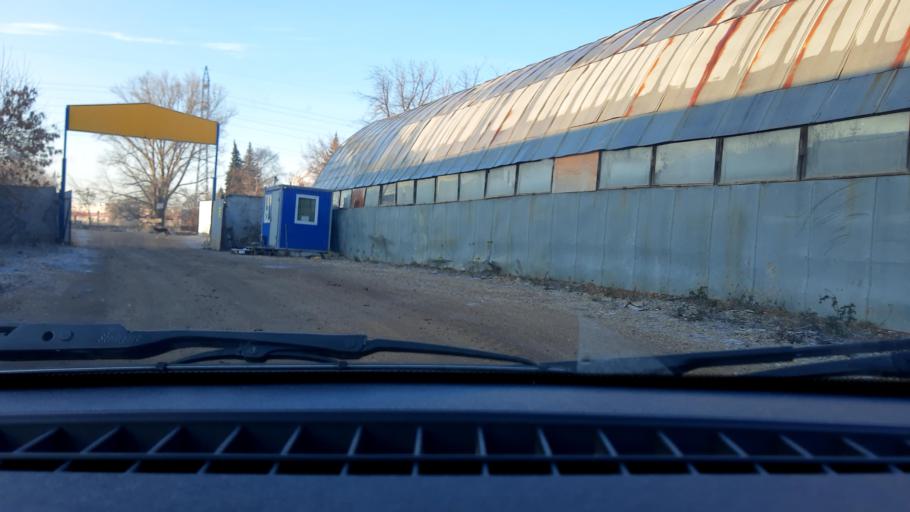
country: RU
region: Bashkortostan
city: Ufa
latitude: 54.7950
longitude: 56.0853
